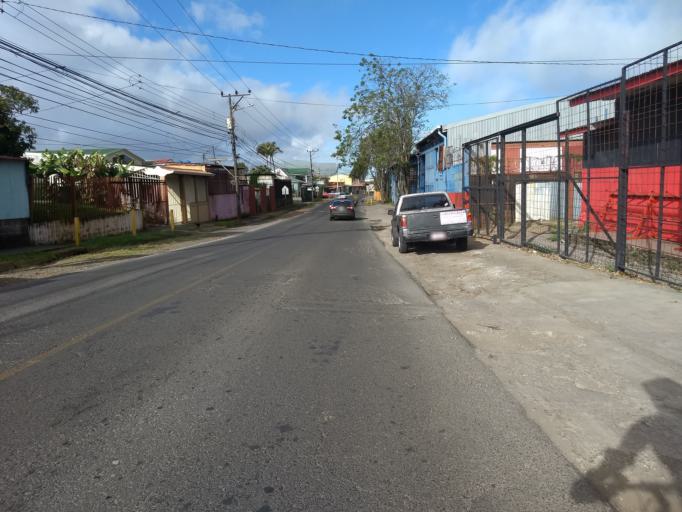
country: CR
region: San Jose
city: San Vicente
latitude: 9.9660
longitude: -84.0390
